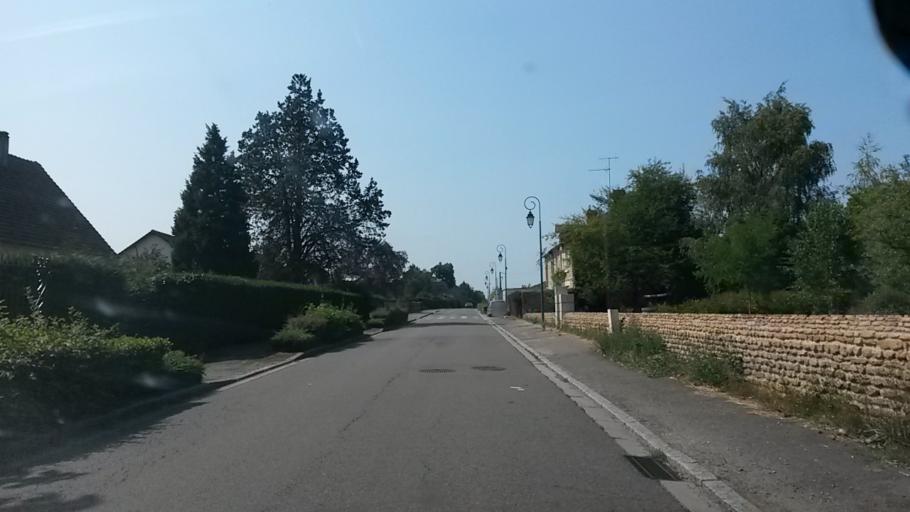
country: FR
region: Pays de la Loire
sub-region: Departement de la Mayenne
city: Saint-Pierre-des-Nids
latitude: 48.3971
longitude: -0.1036
